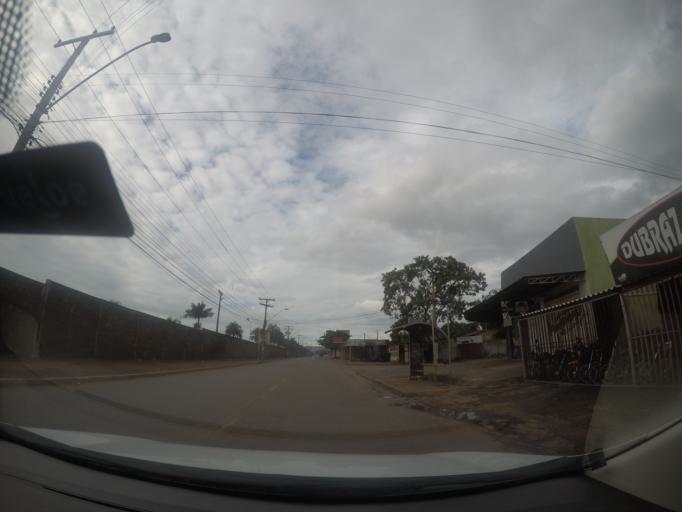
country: BR
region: Goias
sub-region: Goiania
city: Goiania
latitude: -16.6313
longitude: -49.3285
